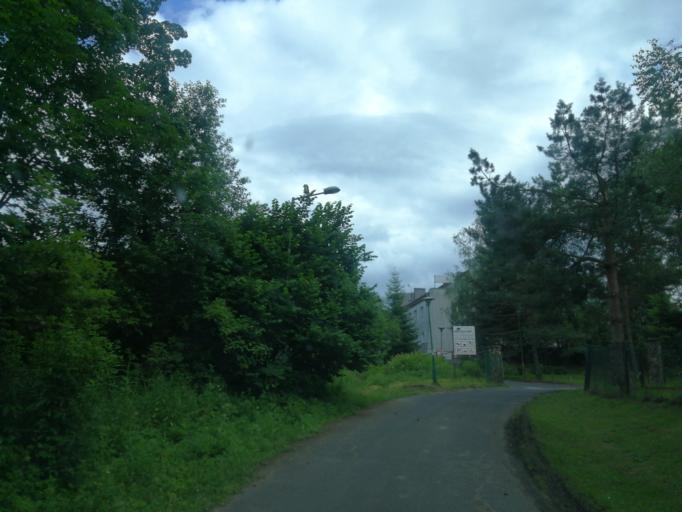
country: PL
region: Subcarpathian Voivodeship
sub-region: Powiat leski
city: Uherce Mineralne
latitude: 49.4302
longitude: 22.4175
